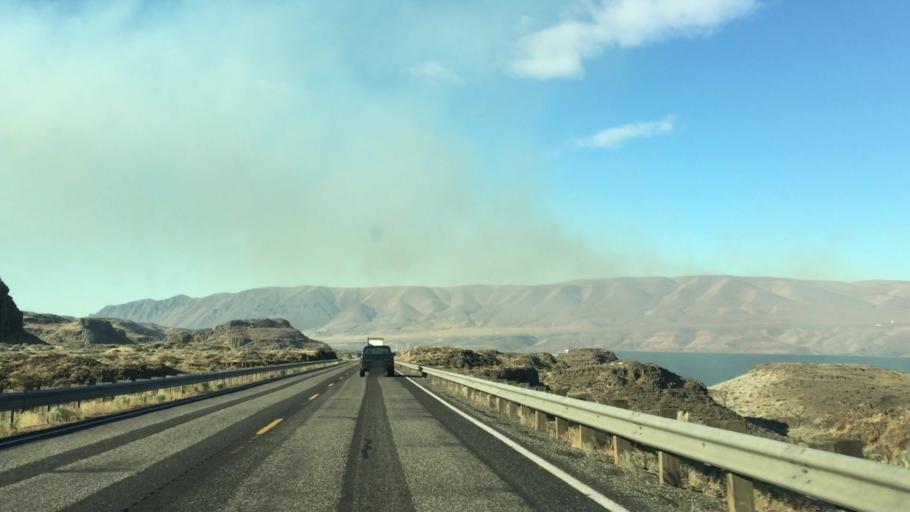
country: US
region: Washington
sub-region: Grant County
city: Mattawa
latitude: 46.9061
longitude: -119.9485
